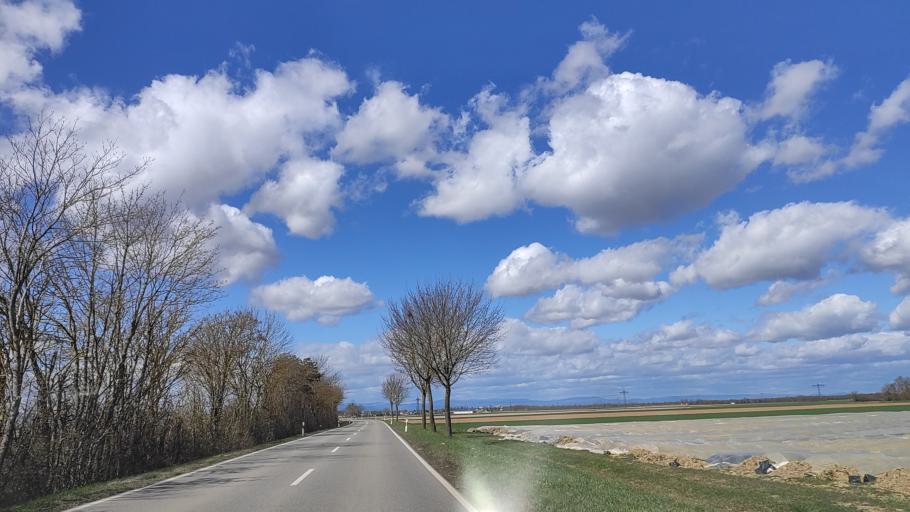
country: DE
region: Baden-Wuerttemberg
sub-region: Freiburg Region
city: Buggingen
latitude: 47.8640
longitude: 7.6105
